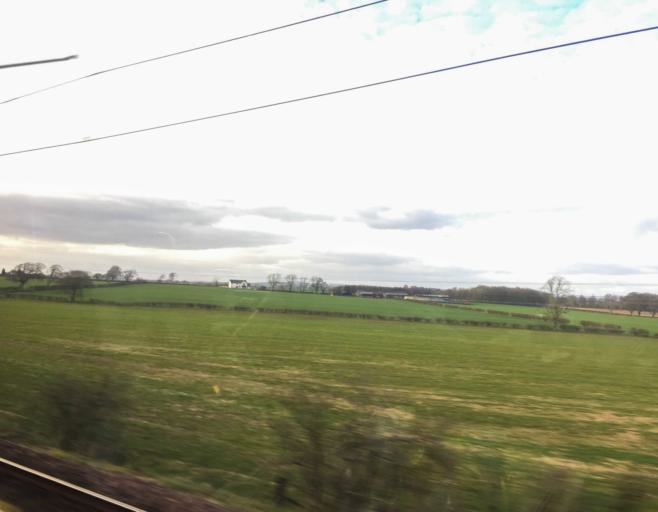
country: GB
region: Scotland
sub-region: Dumfries and Galloway
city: Gretna
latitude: 55.0145
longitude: -3.0648
